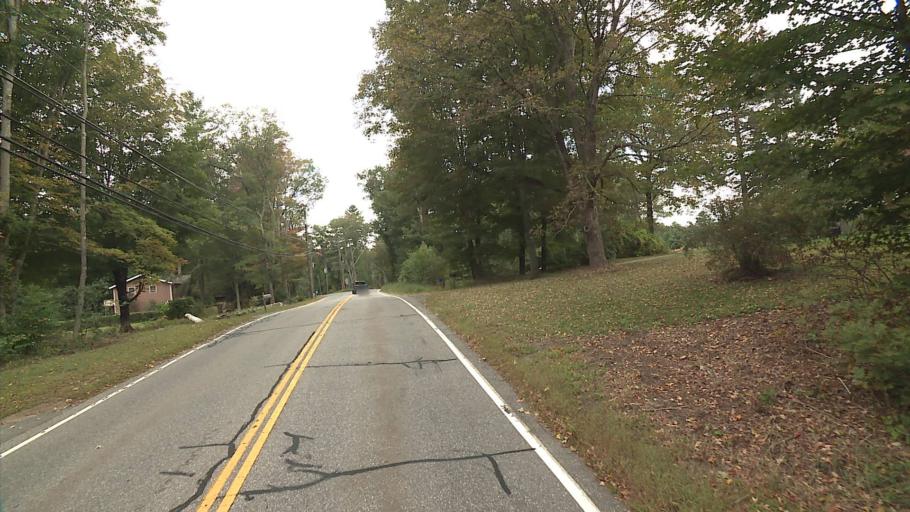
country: US
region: Connecticut
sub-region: Tolland County
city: Storrs
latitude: 41.8381
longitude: -72.2710
